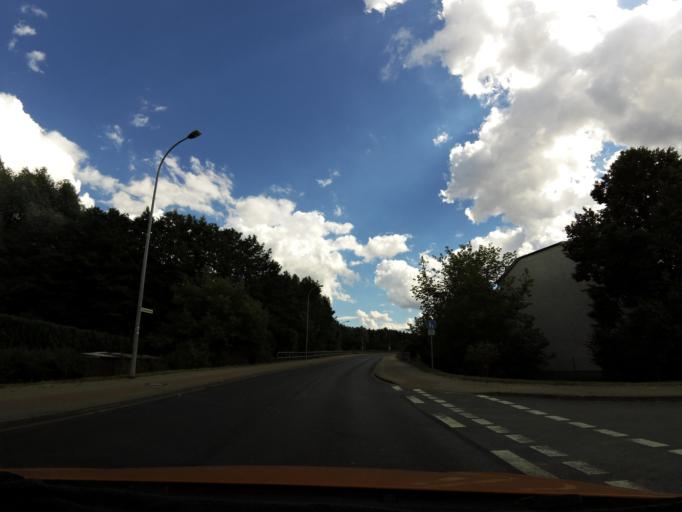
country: DE
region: Brandenburg
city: Konigs Wusterhausen
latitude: 52.3057
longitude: 13.6327
